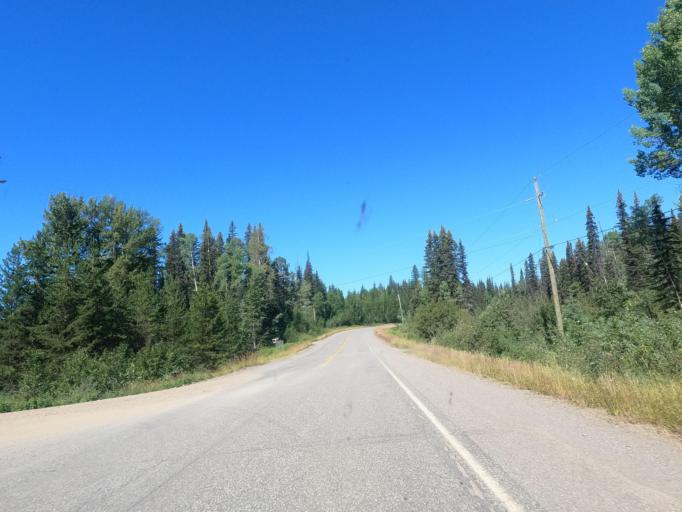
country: CA
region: British Columbia
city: Quesnel
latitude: 53.0211
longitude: -122.0835
